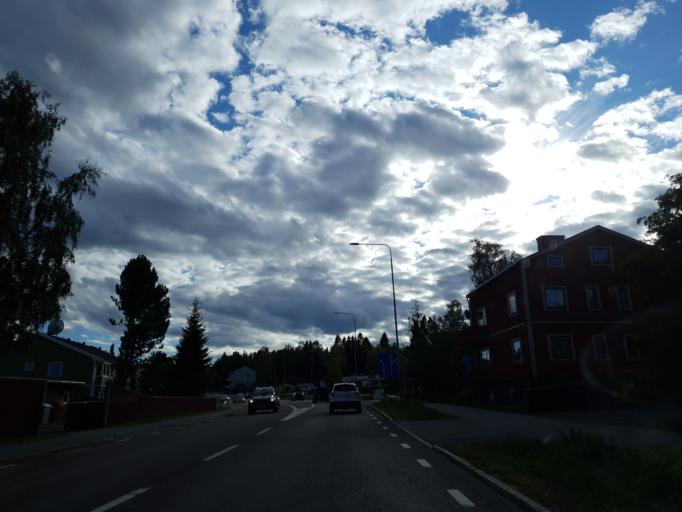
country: SE
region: Vaesternorrland
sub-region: Haernoesands Kommun
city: Haernoesand
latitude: 62.6201
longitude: 17.9130
